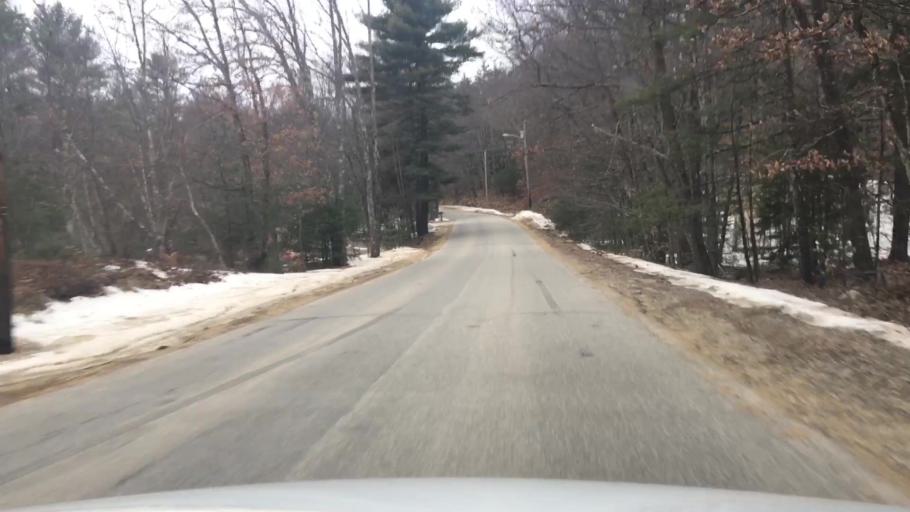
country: US
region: New Hampshire
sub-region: Strafford County
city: Rochester
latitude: 43.3412
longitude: -70.9546
